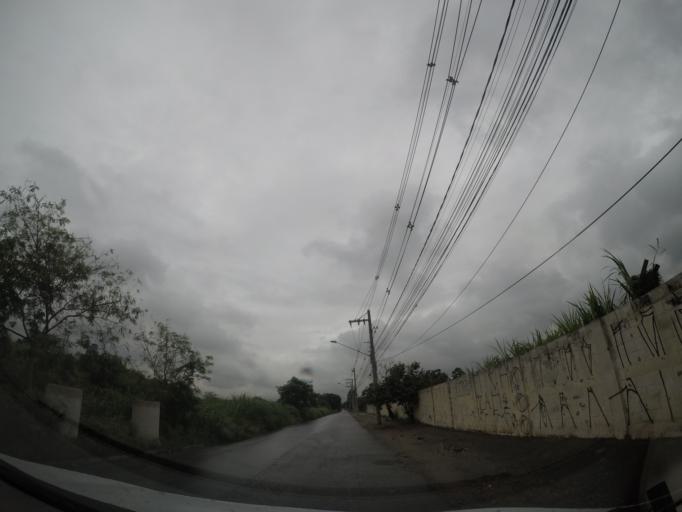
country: BR
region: Sao Paulo
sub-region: Guarulhos
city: Guarulhos
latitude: -23.4774
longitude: -46.4599
